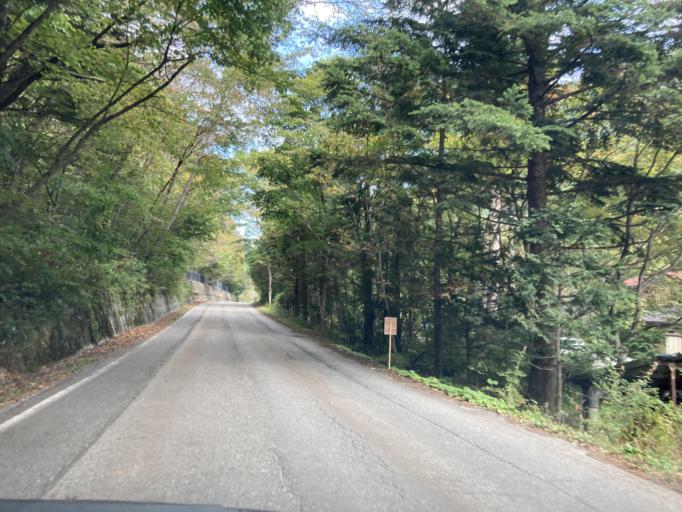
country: JP
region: Nagano
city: Omachi
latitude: 36.4939
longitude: 137.7501
